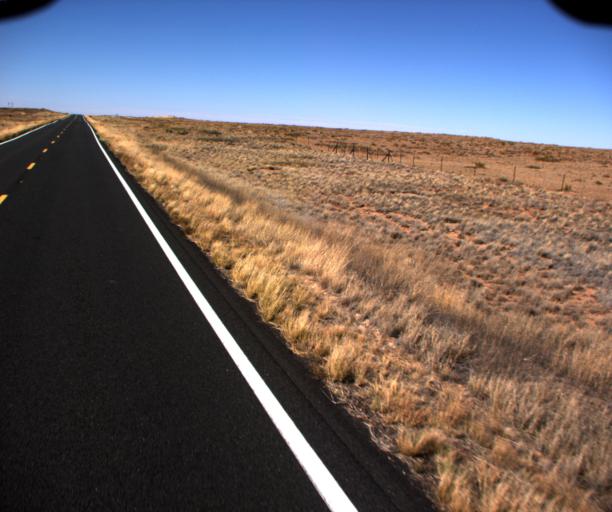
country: US
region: Arizona
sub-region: Coconino County
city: Tuba City
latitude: 35.9910
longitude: -111.0133
